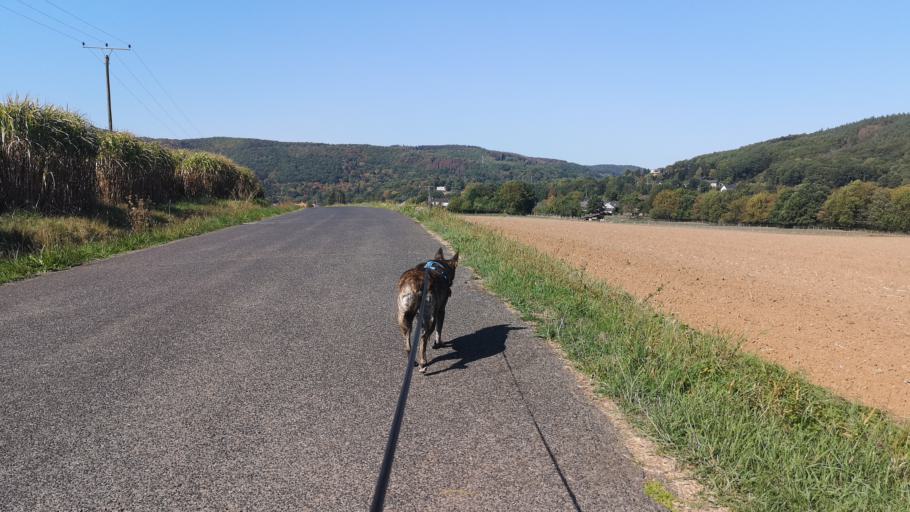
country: DE
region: North Rhine-Westphalia
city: Heimbach
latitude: 50.6553
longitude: 6.4878
